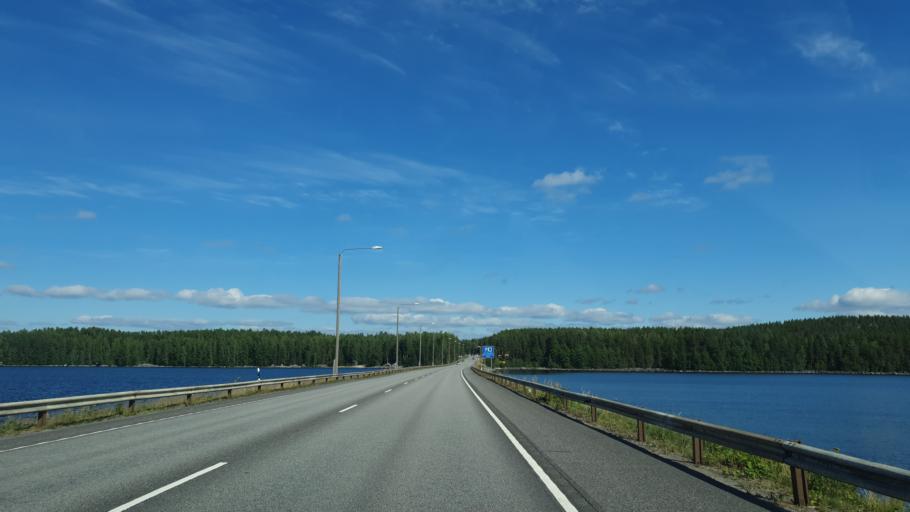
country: FI
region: Central Finland
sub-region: Jyvaeskylae
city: Laukaa
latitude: 62.2359
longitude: 25.9483
